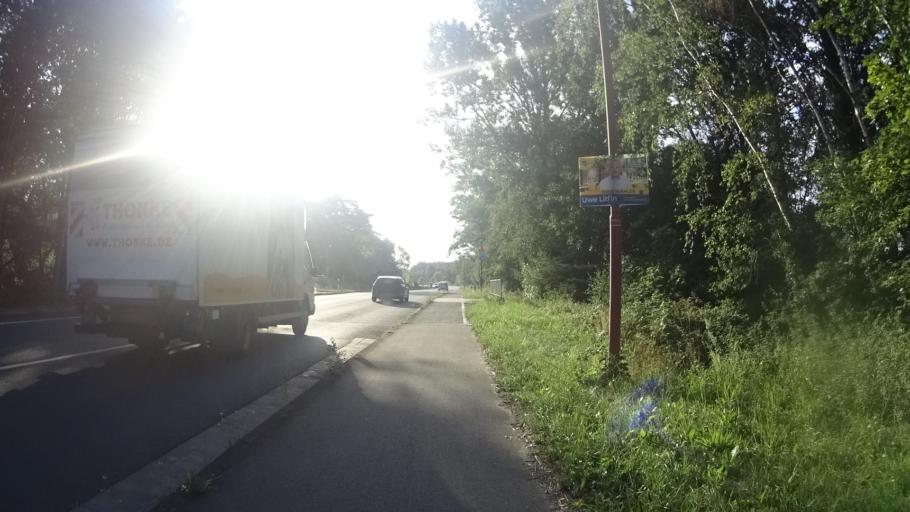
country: DE
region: Brandenburg
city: Premnitz
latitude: 52.5202
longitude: 12.3893
